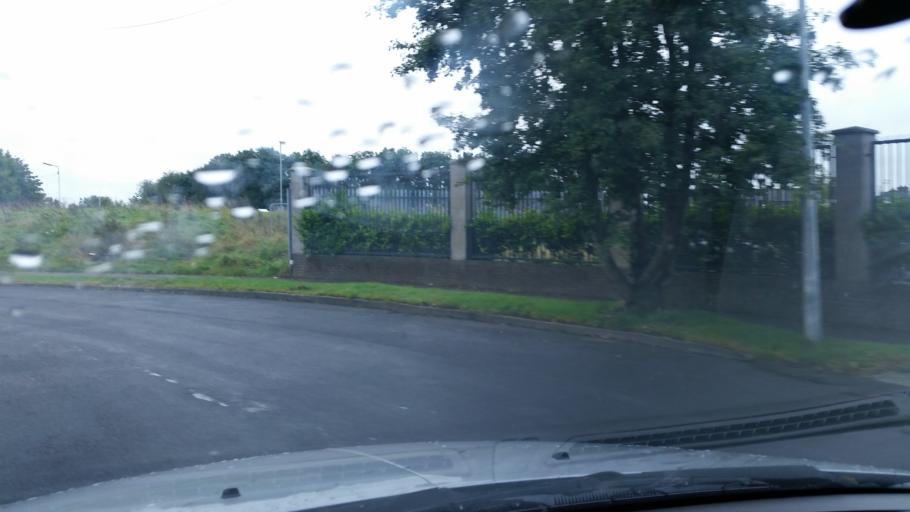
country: IE
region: Leinster
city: Ballymun
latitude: 53.4030
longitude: -6.2724
